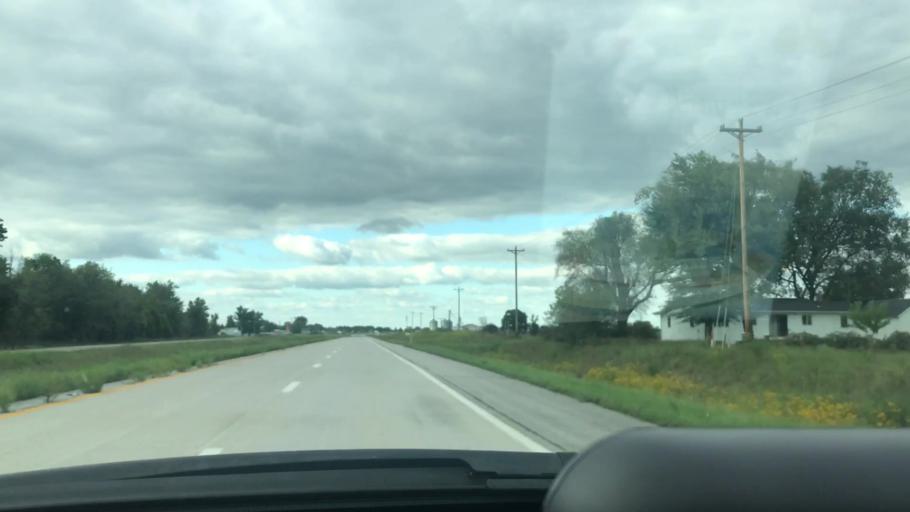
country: US
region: Missouri
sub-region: Benton County
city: Lincoln
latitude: 38.3687
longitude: -93.3387
